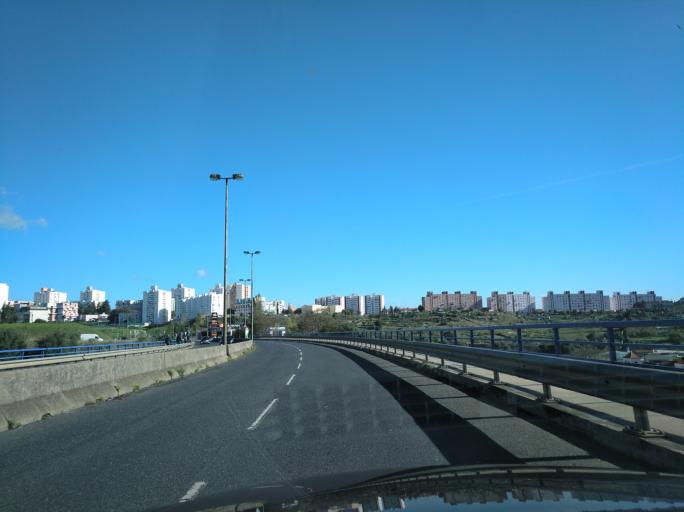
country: PT
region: Lisbon
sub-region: Lisbon
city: Lisbon
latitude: 38.7403
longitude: -9.1210
